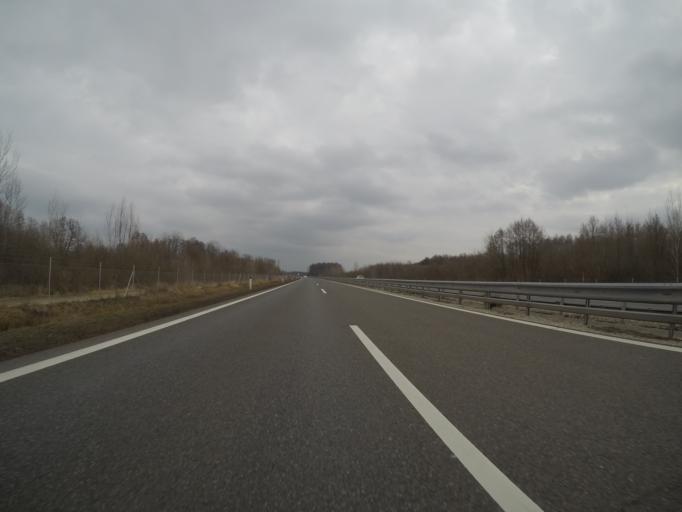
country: SI
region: Velika Polana
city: Velika Polana
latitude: 46.5989
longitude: 16.3508
